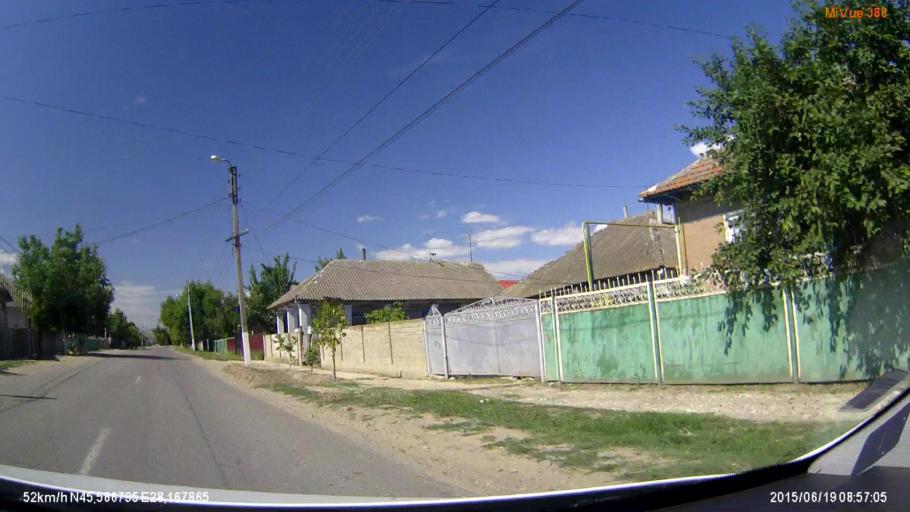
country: MD
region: Cahul
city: Giurgiulesti
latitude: 45.5867
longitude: 28.1679
